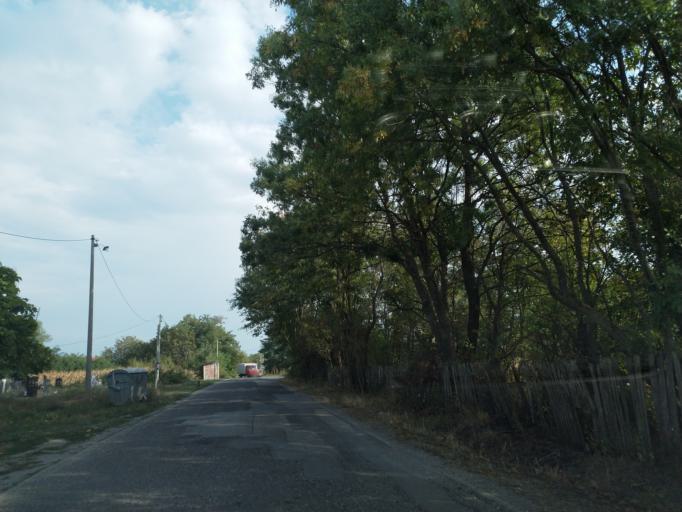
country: RS
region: Central Serbia
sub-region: Pomoravski Okrug
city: Paracin
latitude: 43.8444
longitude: 21.4699
